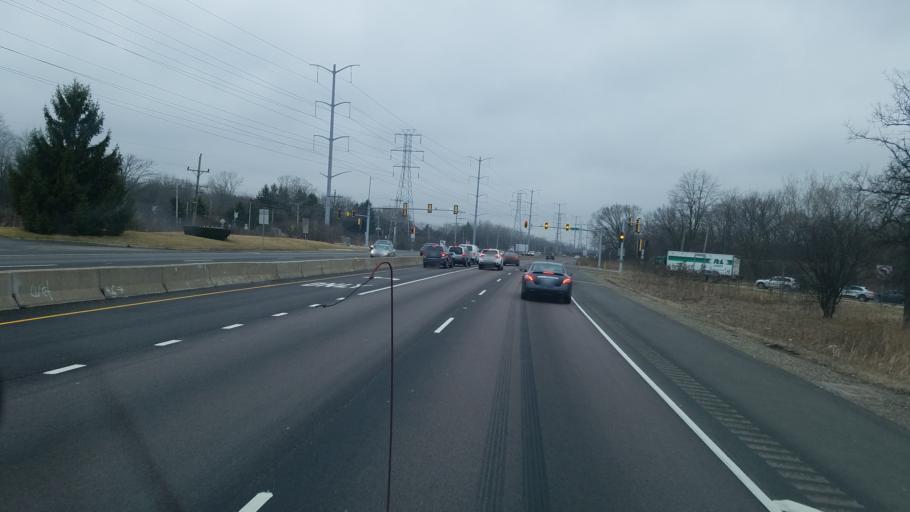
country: US
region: Illinois
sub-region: Lake County
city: Bannockburn
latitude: 42.2173
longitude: -87.8447
